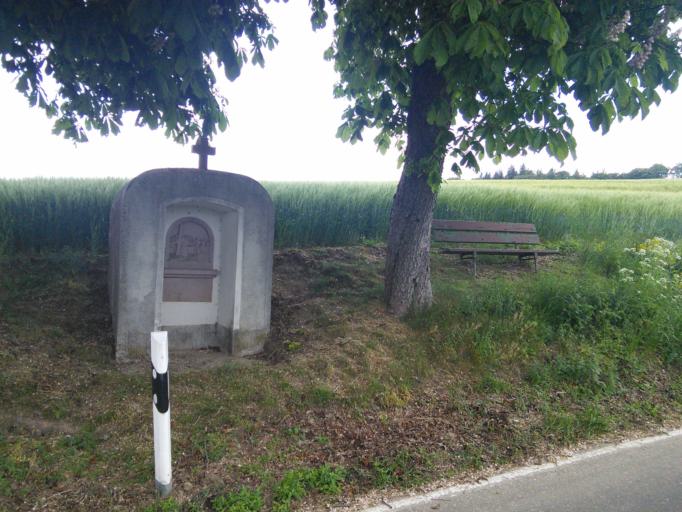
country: DE
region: Rheinland-Pfalz
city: Pantenburg
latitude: 50.0967
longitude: 6.8369
